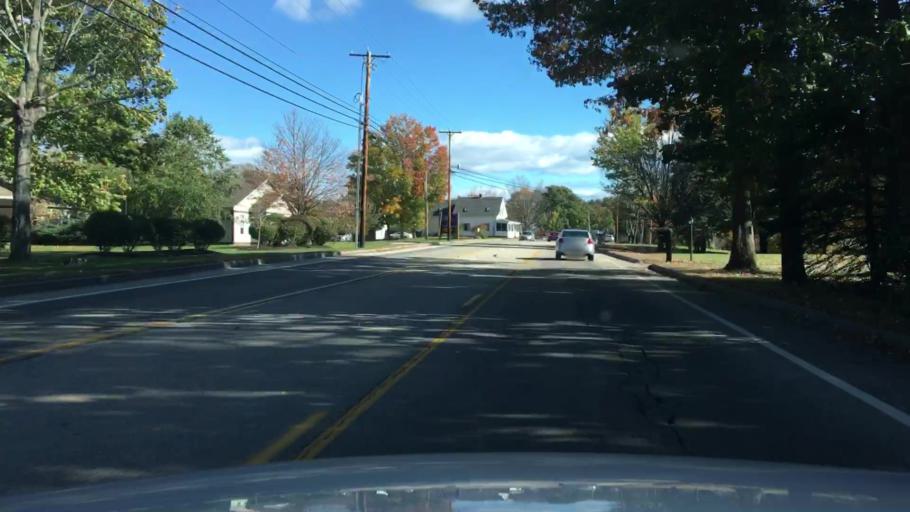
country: US
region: Maine
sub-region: York County
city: South Sanford
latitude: 43.4080
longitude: -70.7367
